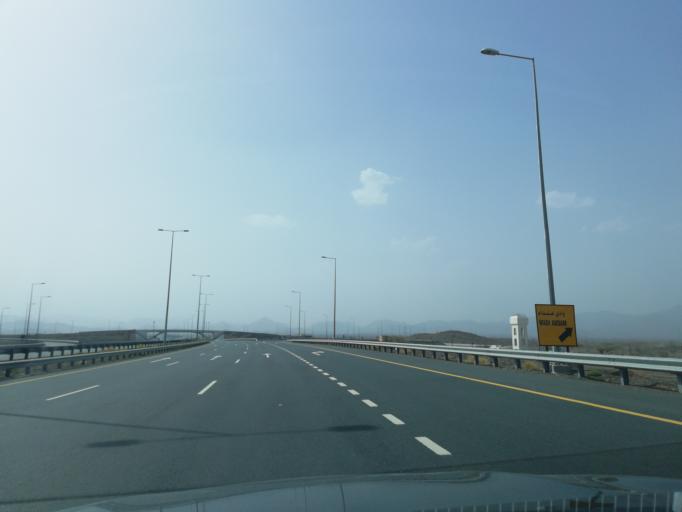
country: OM
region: Muhafazat ad Dakhiliyah
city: Sufalat Sama'il
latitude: 23.0144
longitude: 58.2218
